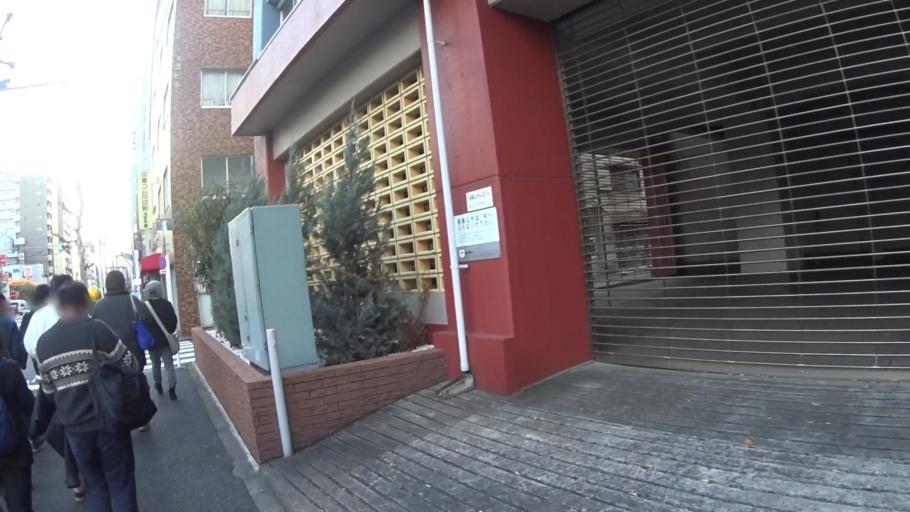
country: JP
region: Tokyo
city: Tokyo
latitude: 35.7016
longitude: 139.7809
